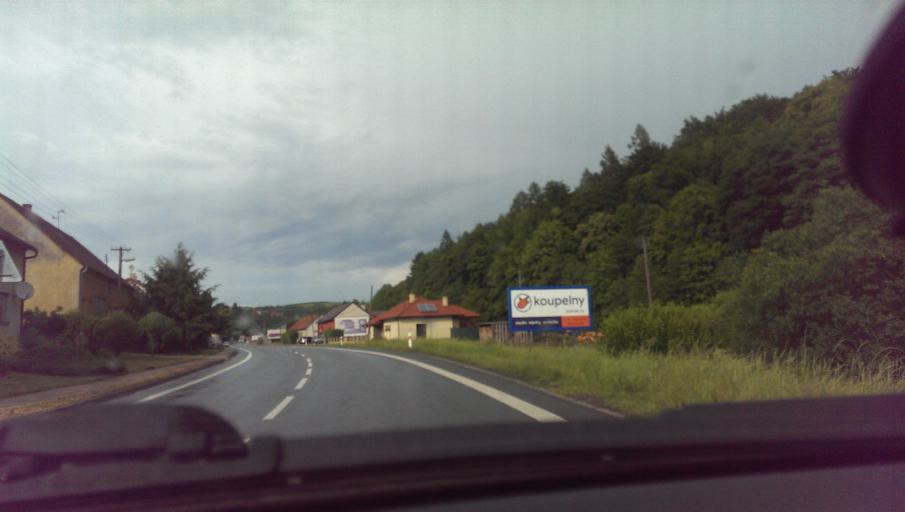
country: CZ
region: Zlin
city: Brezolupy
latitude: 49.1492
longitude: 17.6076
